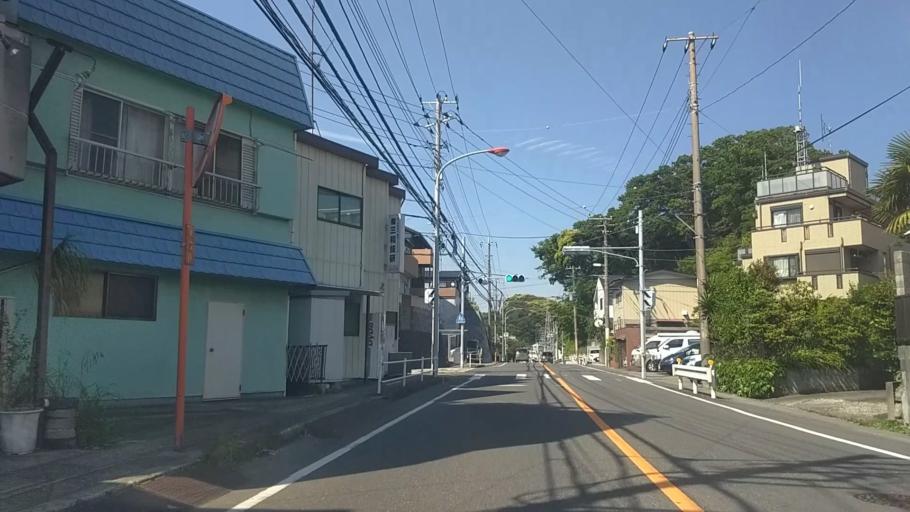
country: JP
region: Kanagawa
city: Kamakura
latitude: 35.3522
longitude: 139.5427
